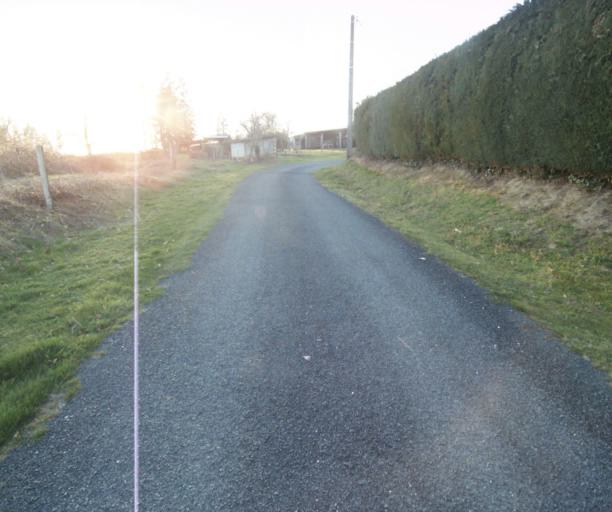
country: FR
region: Limousin
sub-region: Departement de la Correze
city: Uzerche
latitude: 45.3601
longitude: 1.5988
